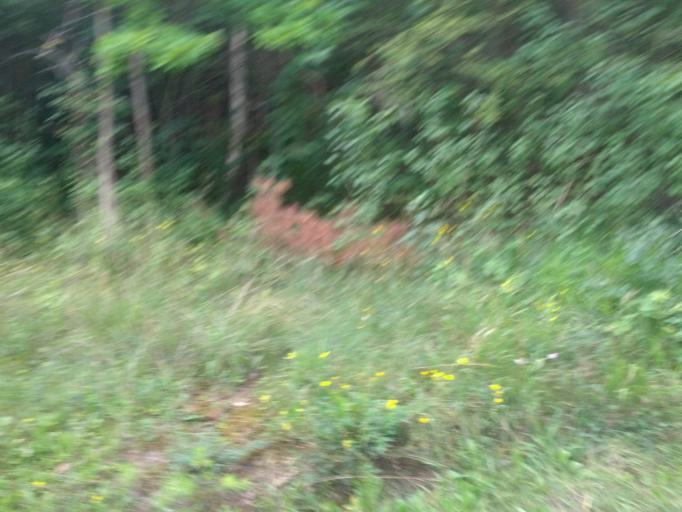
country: DE
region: Thuringia
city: Eisenach
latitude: 50.9867
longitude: 10.3748
